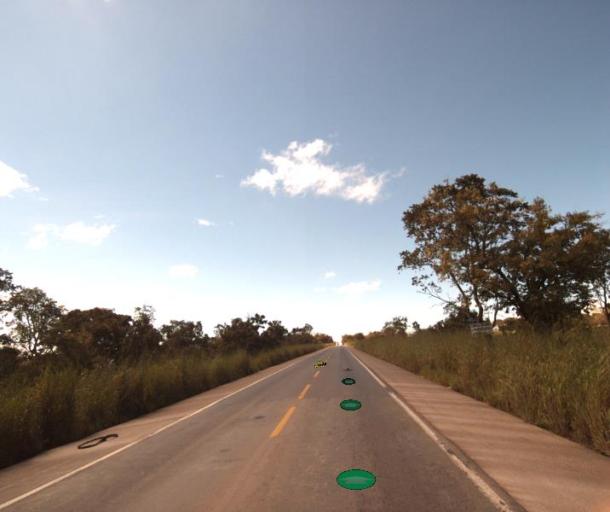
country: BR
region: Goias
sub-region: Uruana
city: Uruana
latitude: -15.5358
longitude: -49.4449
